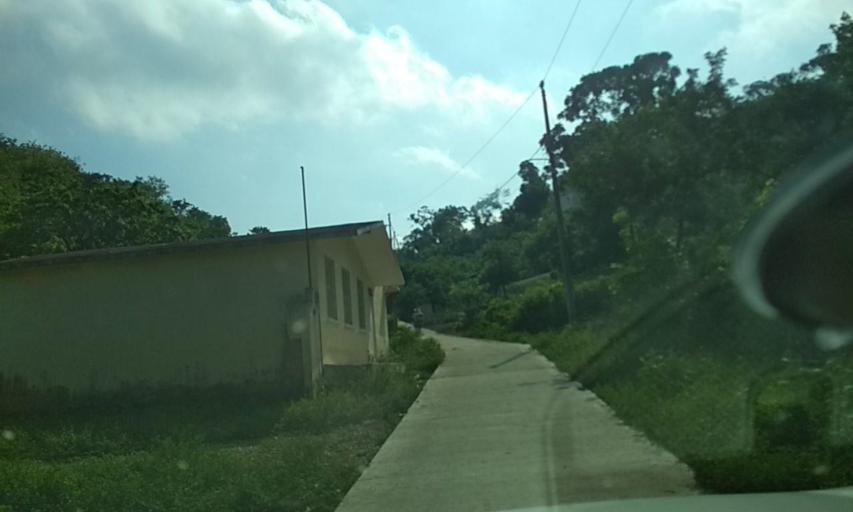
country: MX
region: Veracruz
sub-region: Cazones de Herrera
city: Rancho Nuevo
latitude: 20.6184
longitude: -97.2210
